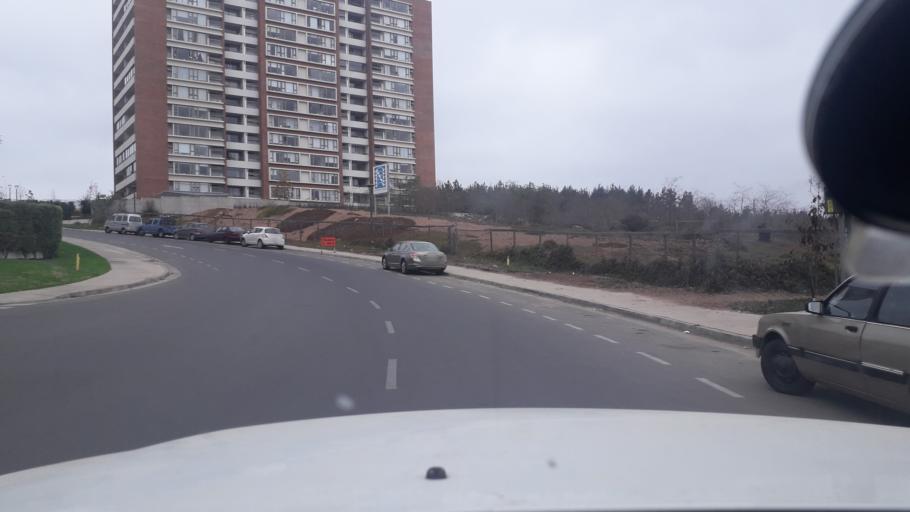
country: CL
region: Valparaiso
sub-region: Provincia de Valparaiso
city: Vina del Mar
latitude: -32.9504
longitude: -71.5402
